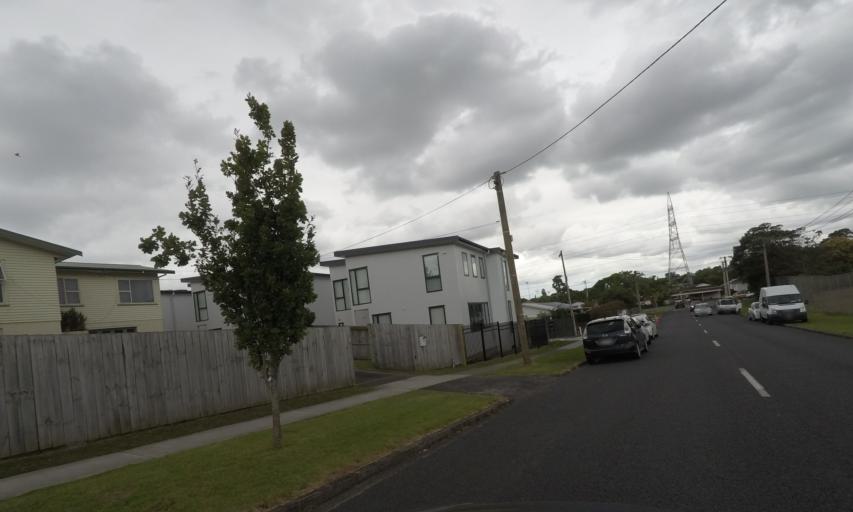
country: NZ
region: Auckland
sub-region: Auckland
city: Waitakere
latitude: -36.9169
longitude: 174.6898
